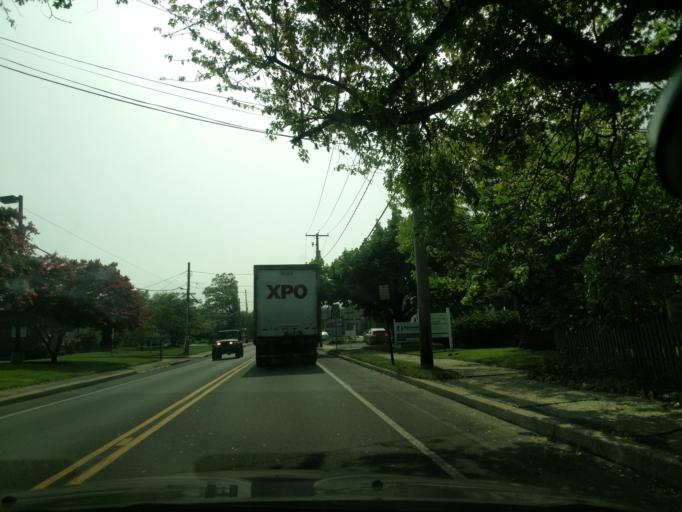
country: US
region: Pennsylvania
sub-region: Chester County
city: Elverson
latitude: 40.1564
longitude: -75.8854
